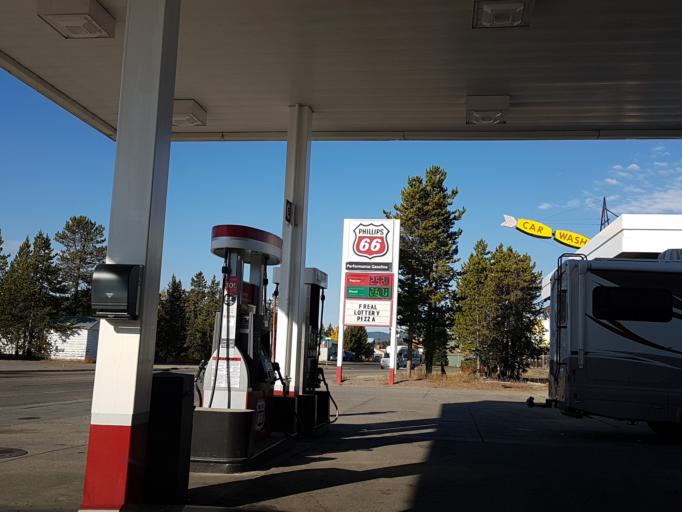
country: US
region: Montana
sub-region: Gallatin County
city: West Yellowstone
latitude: 44.6622
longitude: -111.1050
